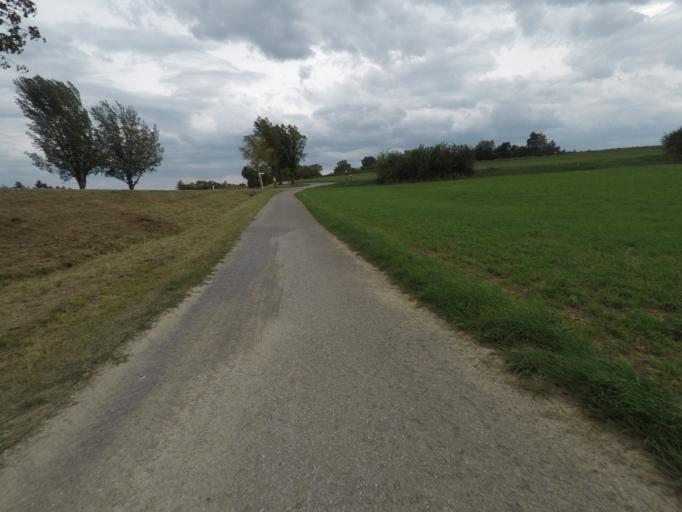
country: DE
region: Baden-Wuerttemberg
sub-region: Regierungsbezirk Stuttgart
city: Herrenberg
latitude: 48.5505
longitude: 8.9083
